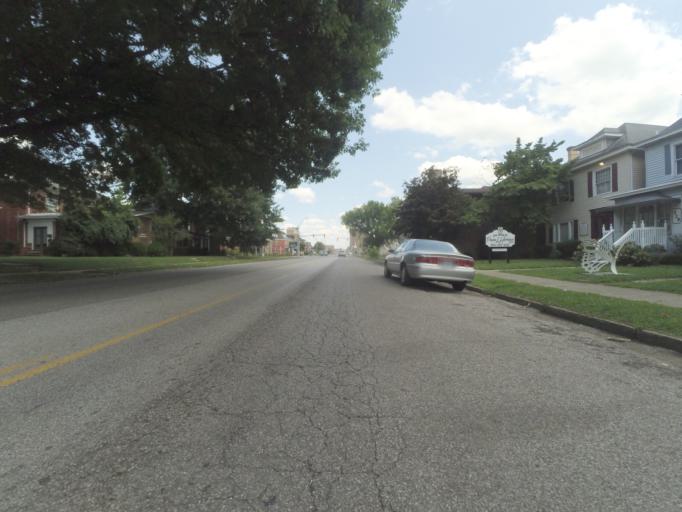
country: US
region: West Virginia
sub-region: Cabell County
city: Huntington
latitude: 38.4169
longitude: -82.4492
